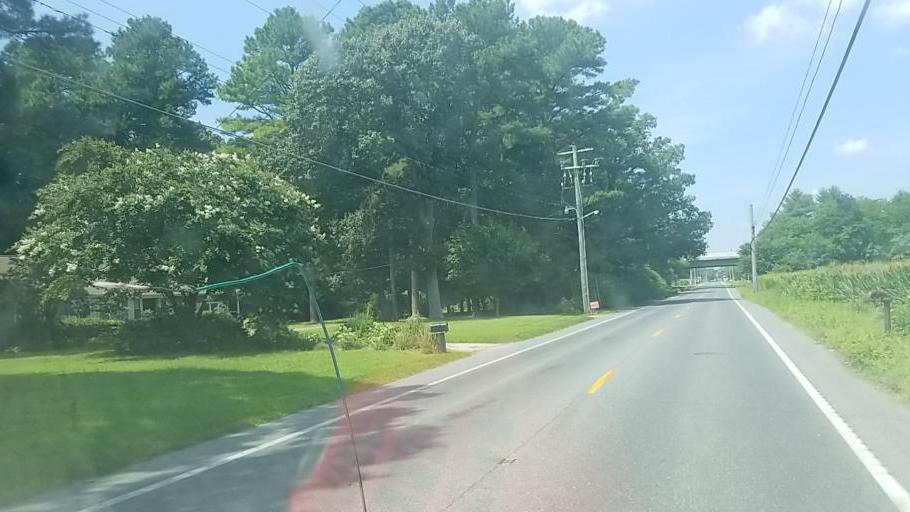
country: US
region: Maryland
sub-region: Wicomico County
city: Salisbury
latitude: 38.3568
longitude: -75.5381
